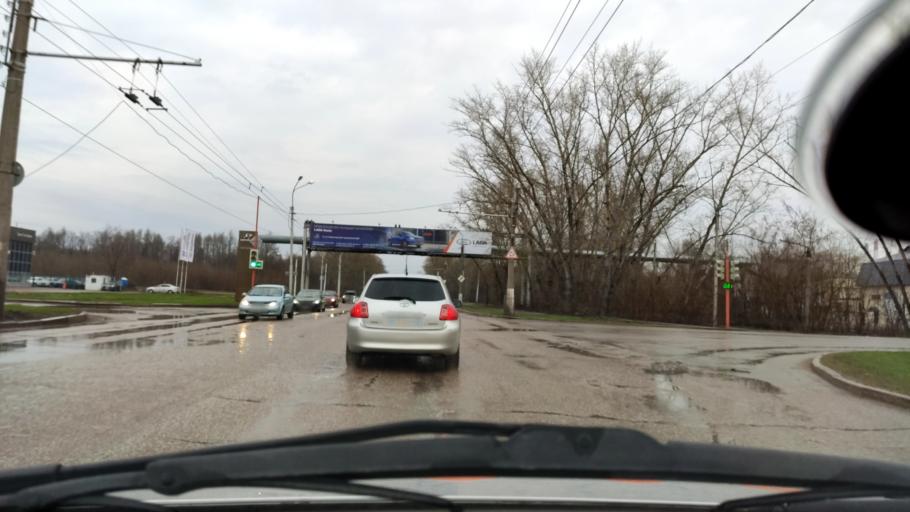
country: RU
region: Bashkortostan
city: Sterlitamak
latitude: 53.6550
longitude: 55.9485
